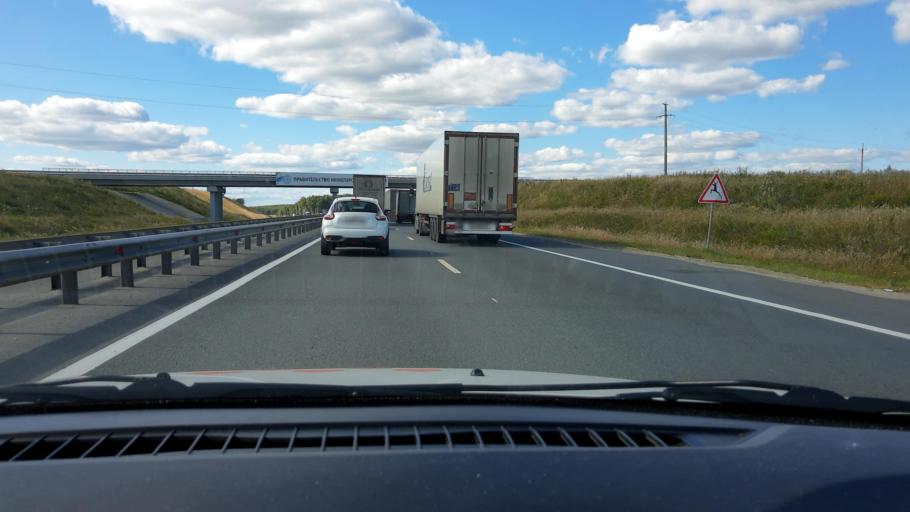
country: RU
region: Nizjnij Novgorod
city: Kstovo
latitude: 56.0911
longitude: 44.0820
